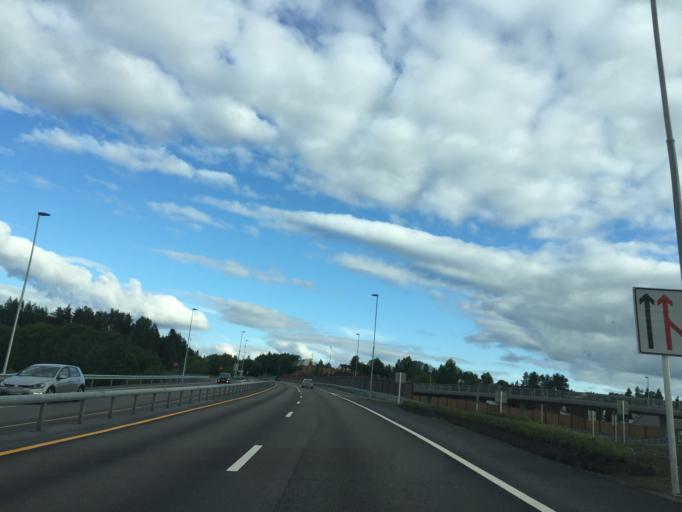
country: NO
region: Akershus
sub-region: Fet
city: Fetsund
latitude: 59.9343
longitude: 11.1359
